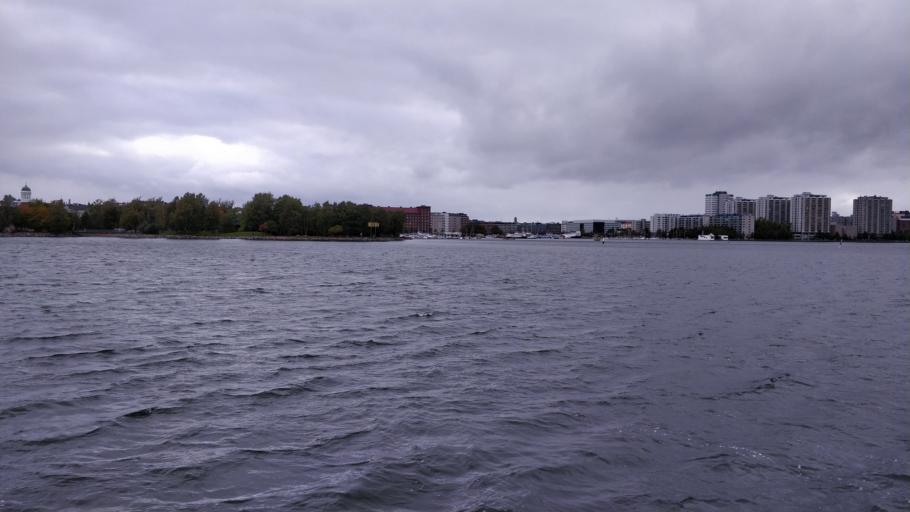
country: FI
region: Uusimaa
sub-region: Helsinki
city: Helsinki
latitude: 60.1738
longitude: 24.9762
